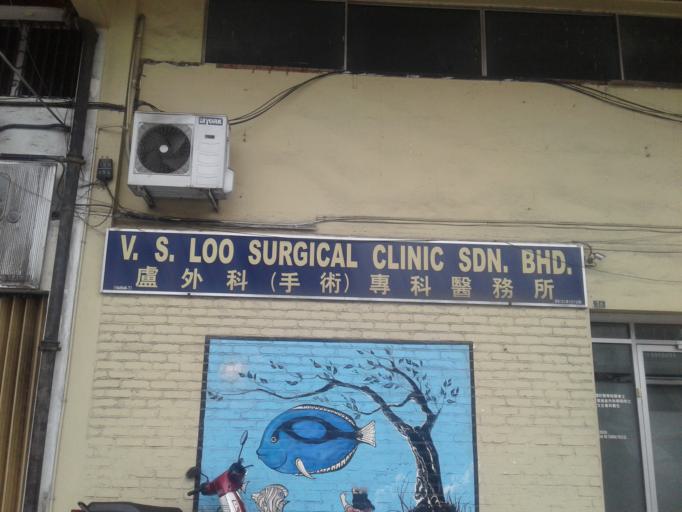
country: MY
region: Perak
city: Ipoh
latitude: 4.6076
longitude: 101.0970
